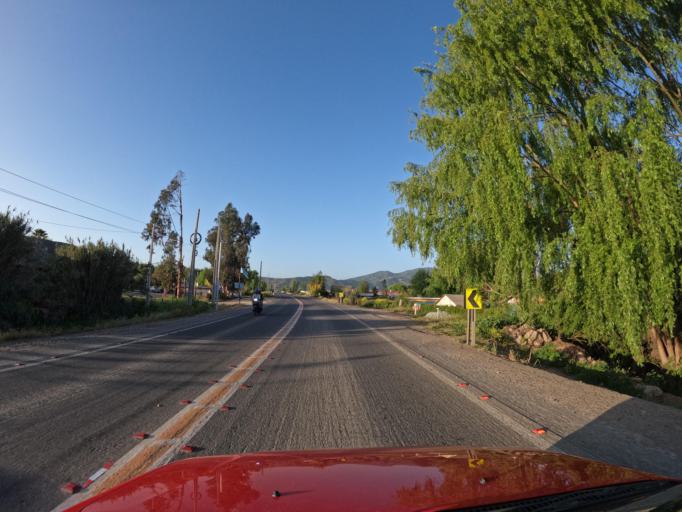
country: CL
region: O'Higgins
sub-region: Provincia de Cachapoal
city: San Vicente
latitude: -34.2933
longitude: -71.3687
